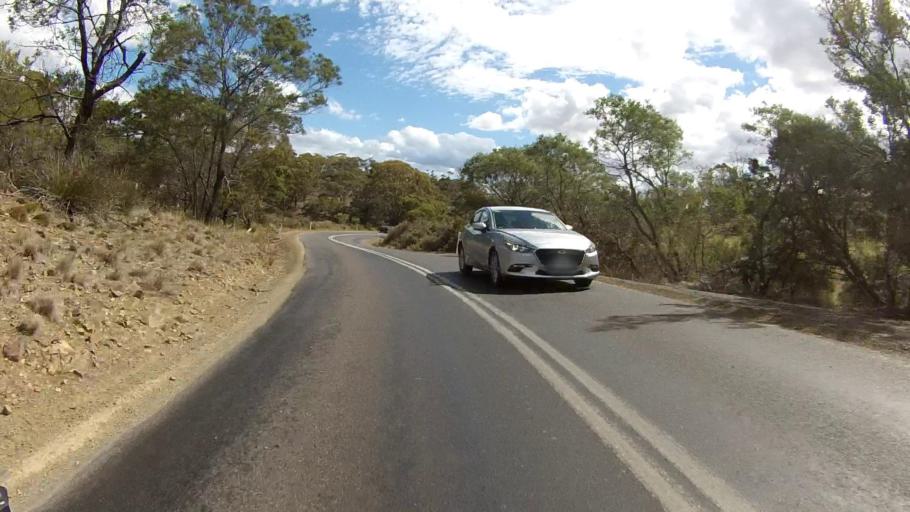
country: AU
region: Tasmania
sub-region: Break O'Day
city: St Helens
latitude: -41.9922
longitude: 148.1169
